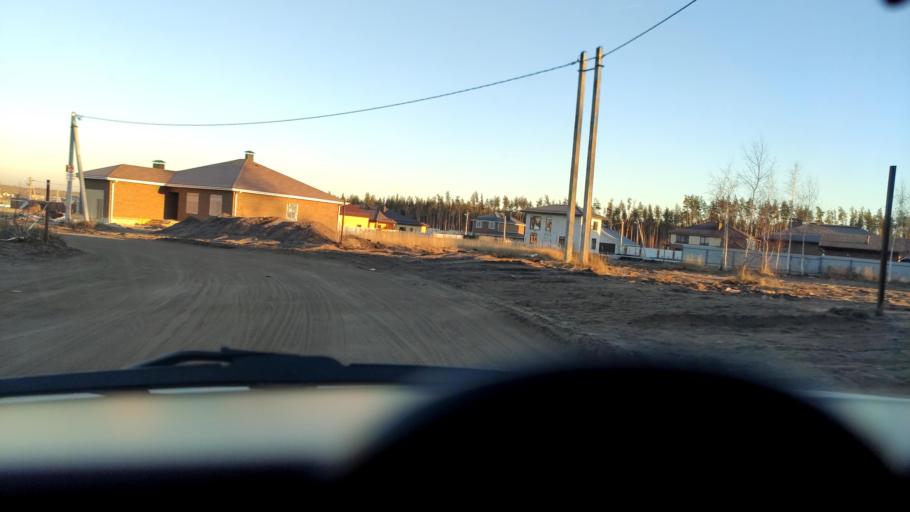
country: RU
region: Voronezj
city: Podgornoye
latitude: 51.7461
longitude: 39.1424
